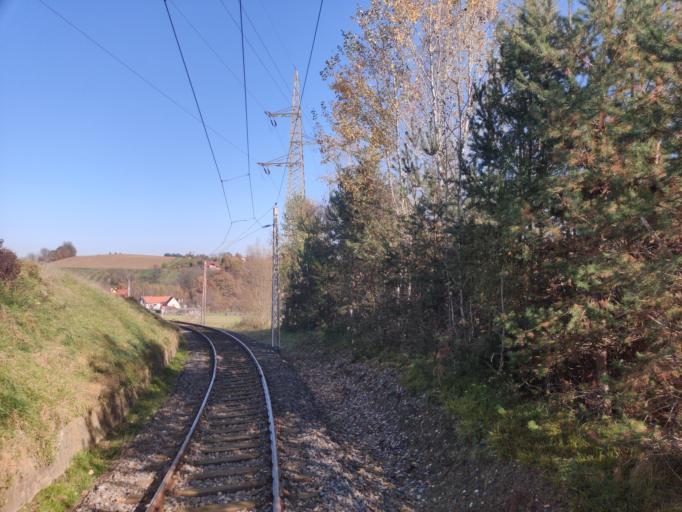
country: AT
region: Styria
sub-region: Politischer Bezirk Suedoststeiermark
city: Maierdorf
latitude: 46.9313
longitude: 15.8554
